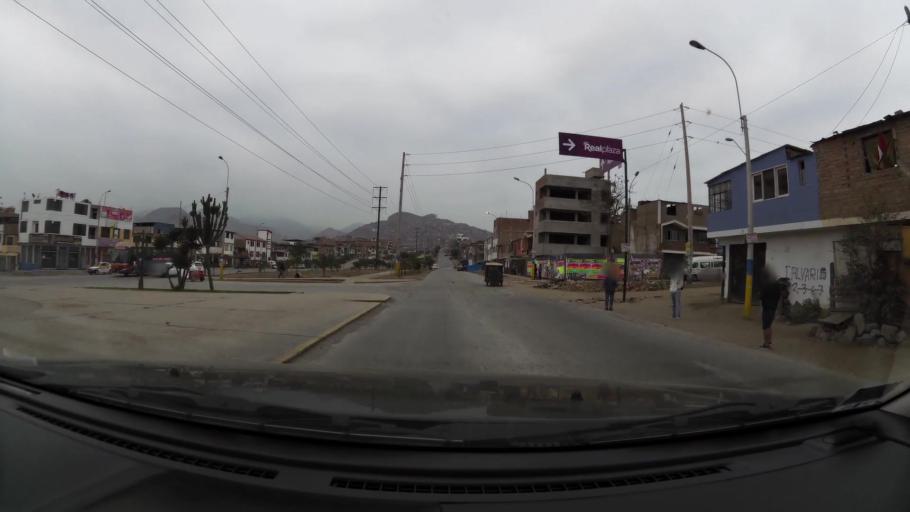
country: PE
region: Lima
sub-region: Lima
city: Surco
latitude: -12.1933
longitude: -76.9490
